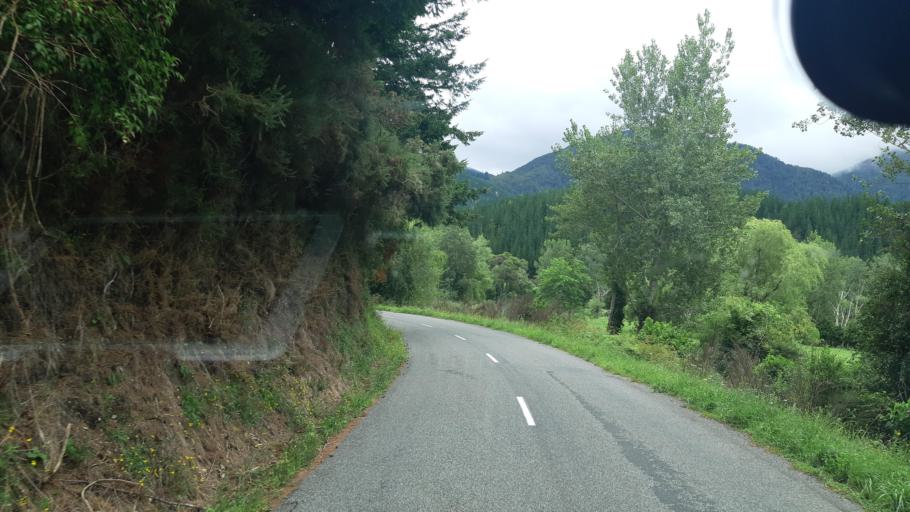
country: NZ
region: Marlborough
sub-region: Marlborough District
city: Blenheim
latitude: -41.4516
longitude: 173.7206
